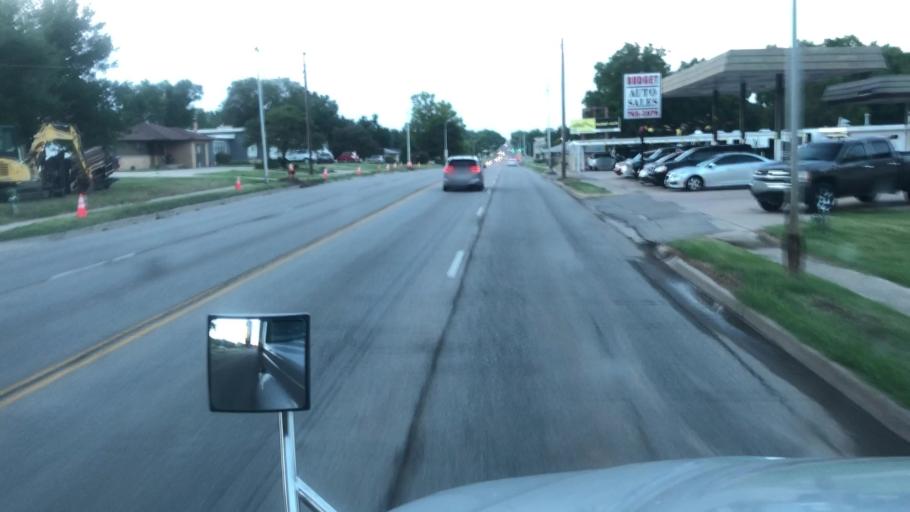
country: US
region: Oklahoma
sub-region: Kay County
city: Ponca City
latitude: 36.7048
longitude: -97.0673
